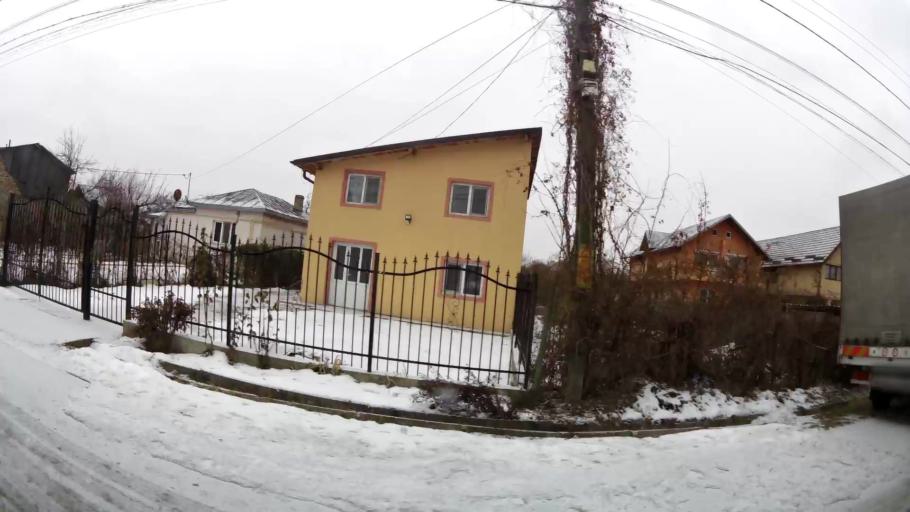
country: RO
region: Dambovita
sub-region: Comuna Aninoasa
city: Viforata
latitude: 44.9452
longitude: 25.4675
